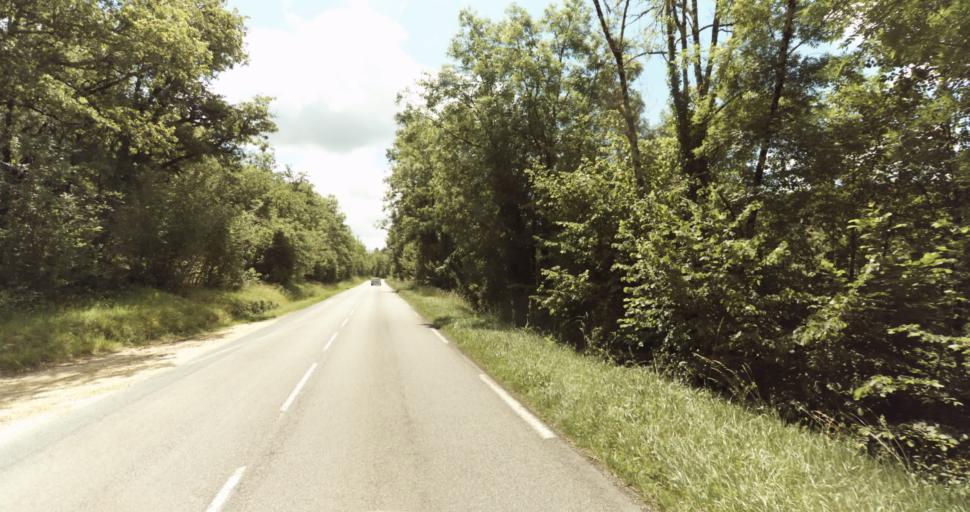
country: FR
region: Aquitaine
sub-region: Departement de la Dordogne
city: Lalinde
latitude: 44.8011
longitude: 0.7373
